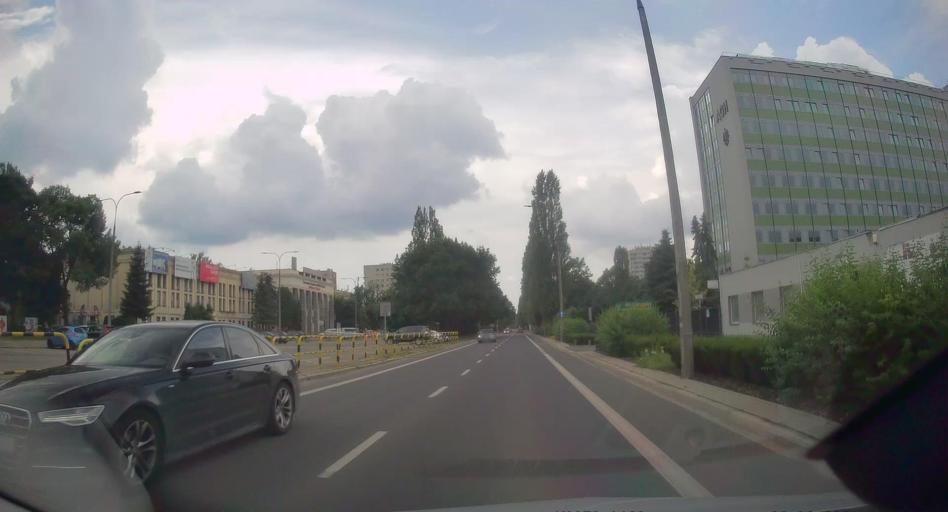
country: PL
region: Lesser Poland Voivodeship
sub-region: Krakow
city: Krakow
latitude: 50.0661
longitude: 19.9119
